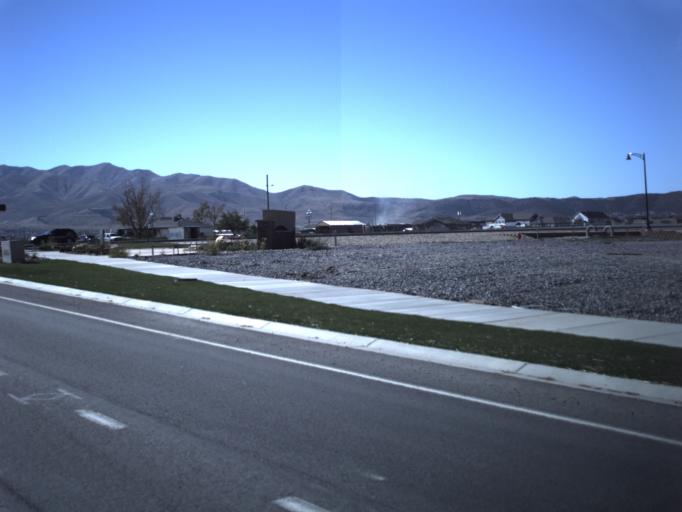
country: US
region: Utah
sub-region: Utah County
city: Saratoga Springs
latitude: 40.3736
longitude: -111.9165
